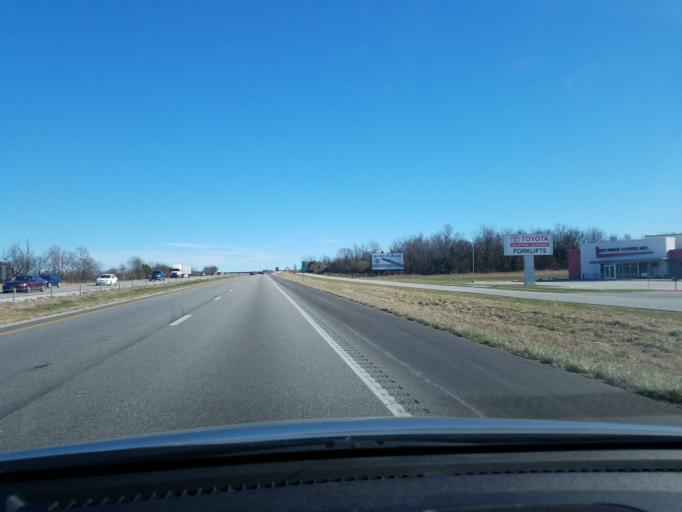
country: US
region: Missouri
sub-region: Greene County
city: Strafford
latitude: 37.2501
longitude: -93.1948
